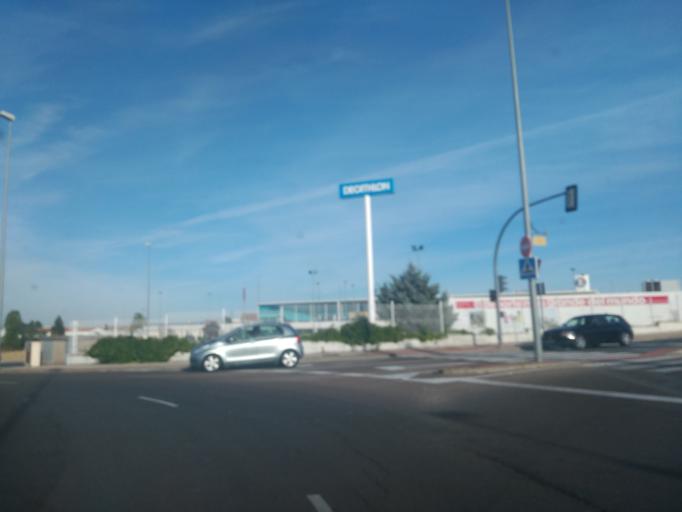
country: ES
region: Castille and Leon
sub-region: Provincia de Salamanca
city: Santa Marta de Tormes
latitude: 40.9466
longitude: -5.6422
